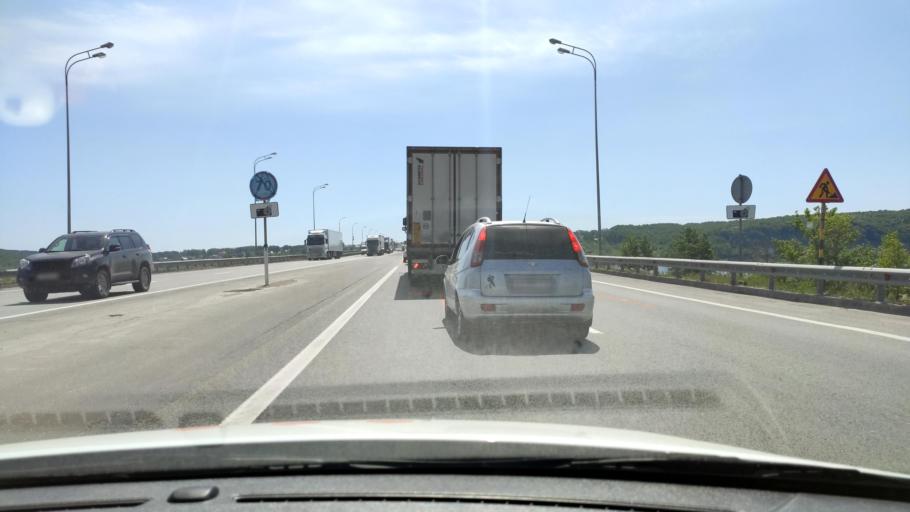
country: RU
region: Tatarstan
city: Osinovo
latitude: 55.7919
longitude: 48.8408
